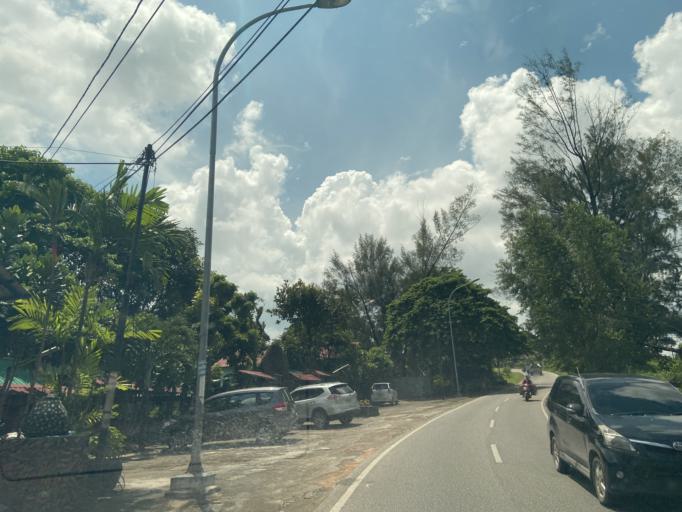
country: SG
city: Singapore
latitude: 1.1533
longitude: 104.0084
